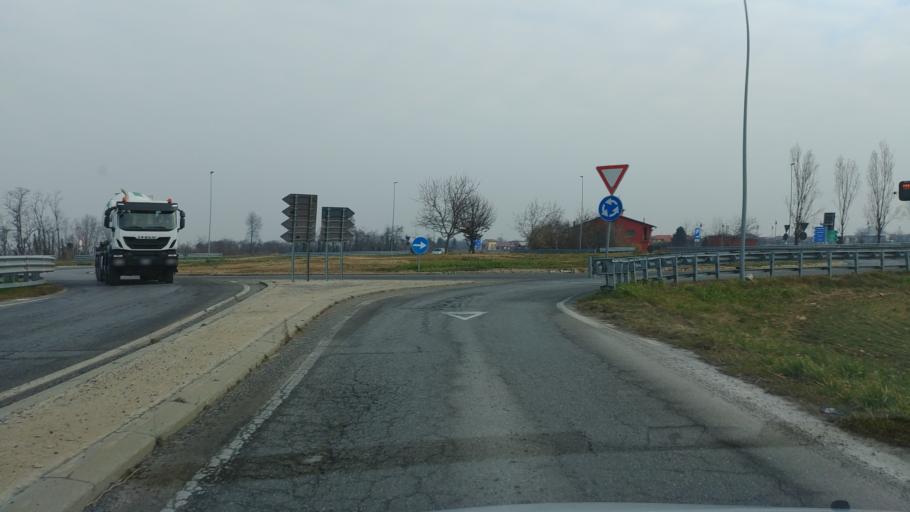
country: IT
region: Piedmont
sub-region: Provincia di Cuneo
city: Montanera
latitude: 44.4815
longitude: 7.6880
